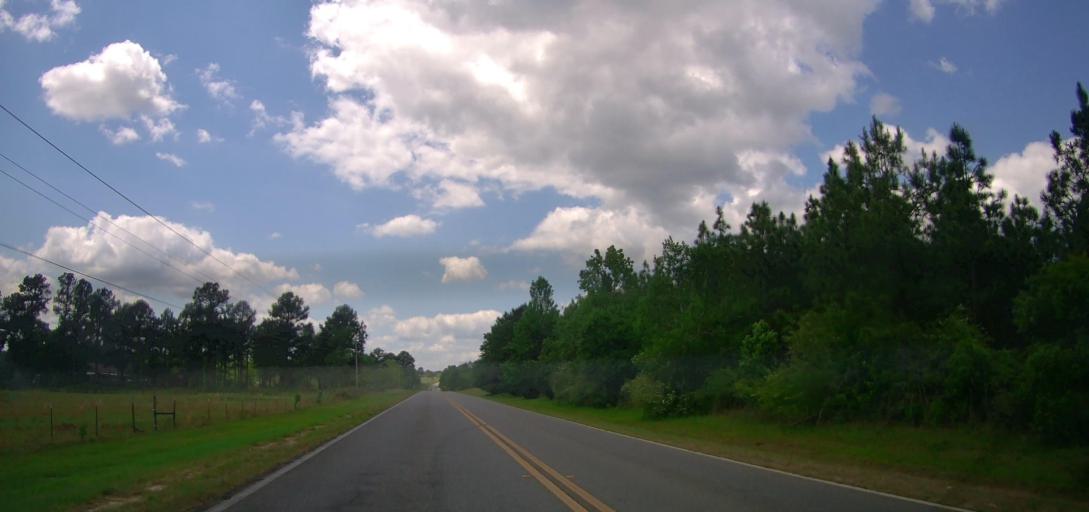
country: US
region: Georgia
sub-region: Laurens County
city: East Dublin
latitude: 32.5185
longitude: -82.7878
